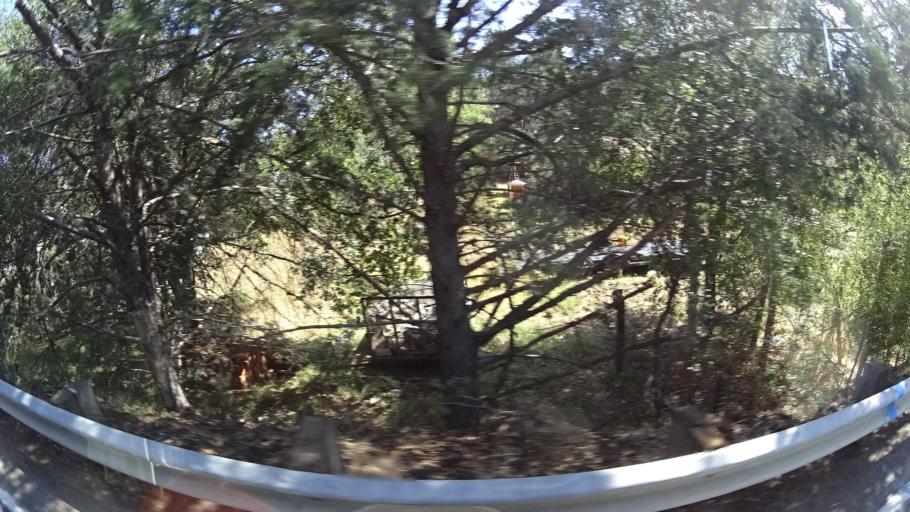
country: US
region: California
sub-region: Lake County
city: Clearlake Oaks
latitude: 39.0490
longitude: -122.5811
